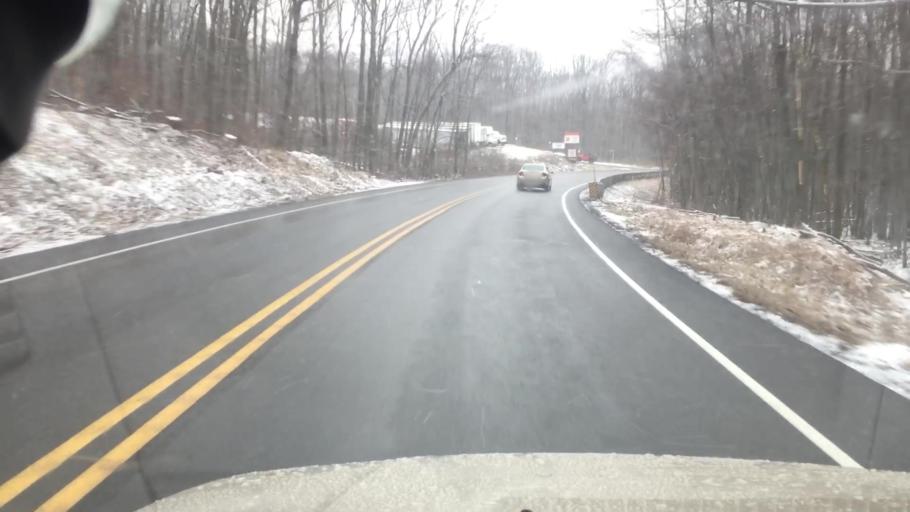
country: US
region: Pennsylvania
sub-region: Luzerne County
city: Conyngham
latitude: 41.0310
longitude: -76.0821
